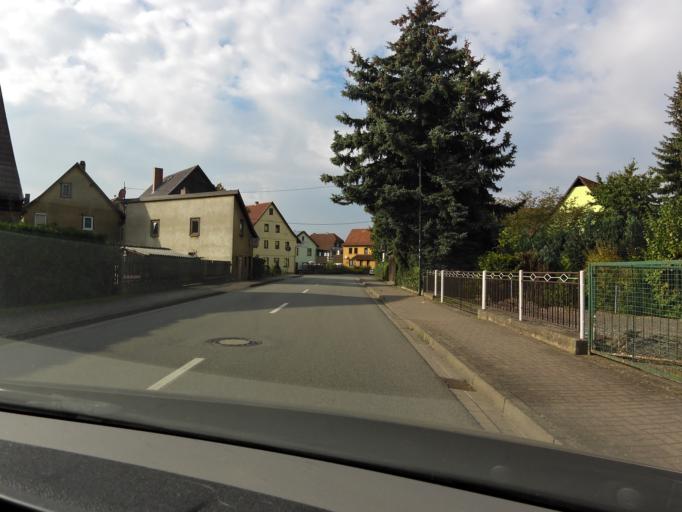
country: DE
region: Thuringia
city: Breitungen
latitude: 50.7534
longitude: 10.3443
